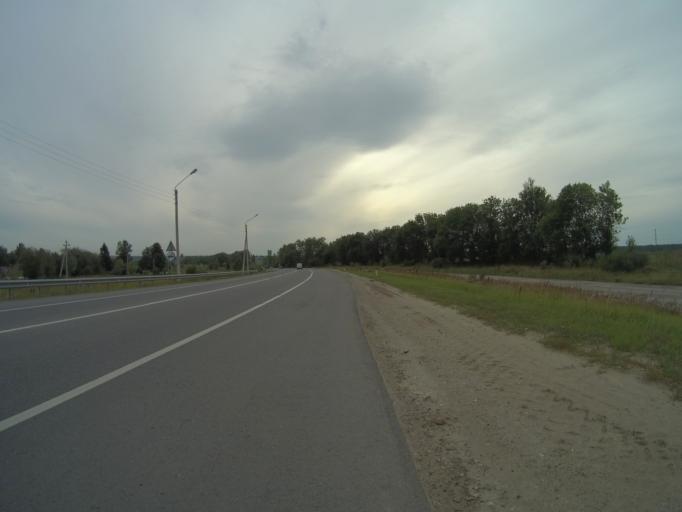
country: RU
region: Vladimir
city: Orgtrud
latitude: 56.2113
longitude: 40.5832
